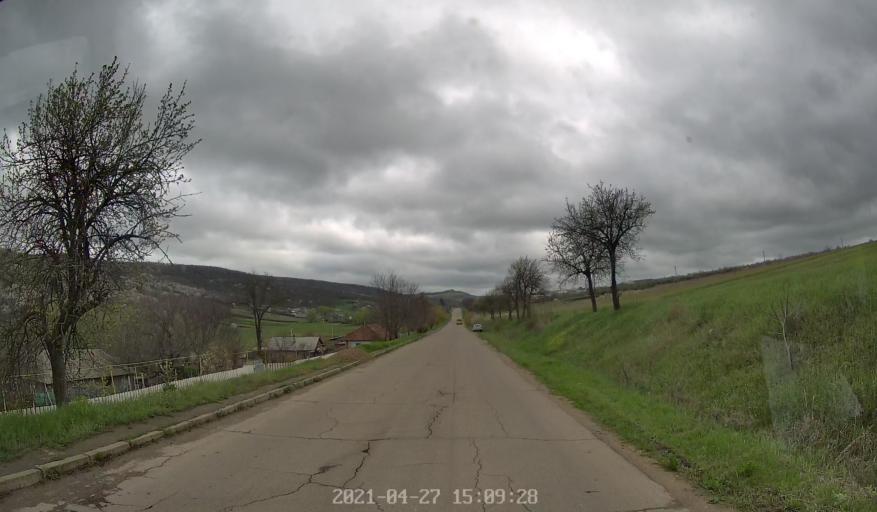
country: MD
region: Chisinau
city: Vadul lui Voda
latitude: 47.0495
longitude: 29.0339
